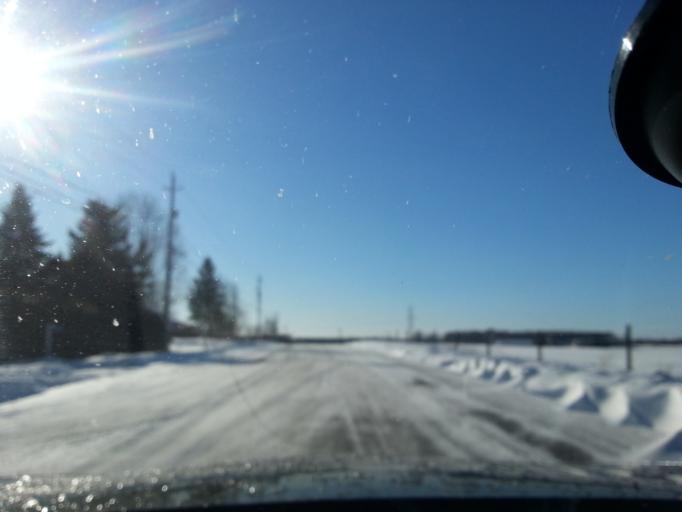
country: CA
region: Ontario
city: Clarence-Rockland
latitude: 45.3005
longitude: -75.3961
